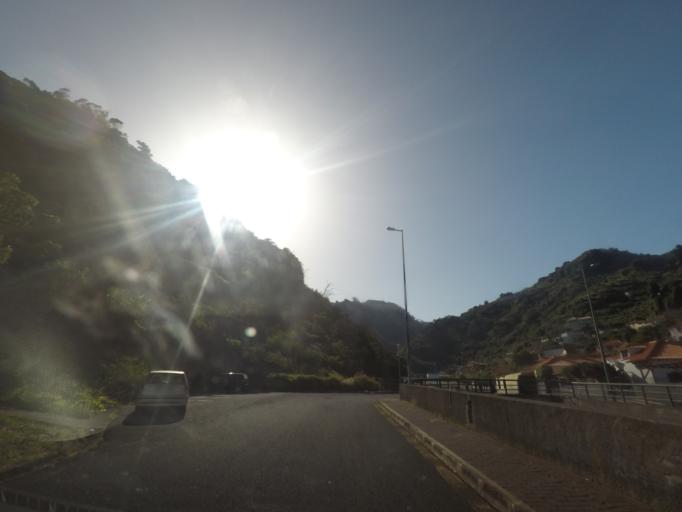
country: PT
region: Madeira
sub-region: Santa Cruz
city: Santa Cruz
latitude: 32.6903
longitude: -16.7979
